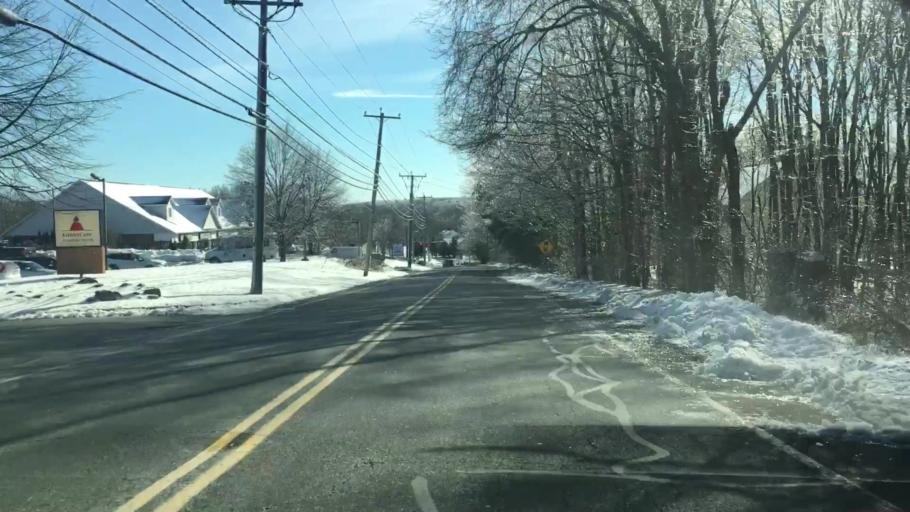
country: US
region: Connecticut
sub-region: Fairfield County
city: Trumbull
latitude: 41.3162
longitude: -73.2193
